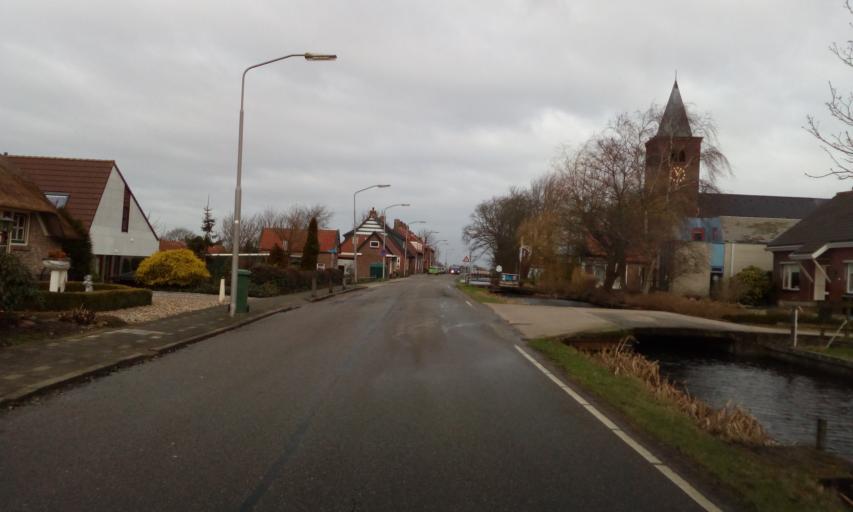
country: NL
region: South Holland
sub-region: Gemeente Nieuwkoop
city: Nieuwkoop
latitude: 52.1927
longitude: 4.7739
